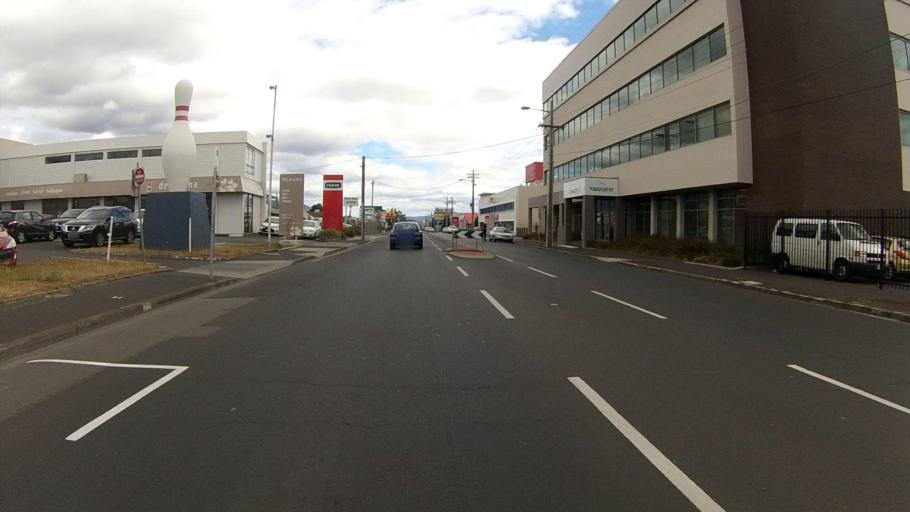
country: AU
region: Tasmania
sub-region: Glenorchy
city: Moonah
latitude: -42.8430
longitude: 147.2922
